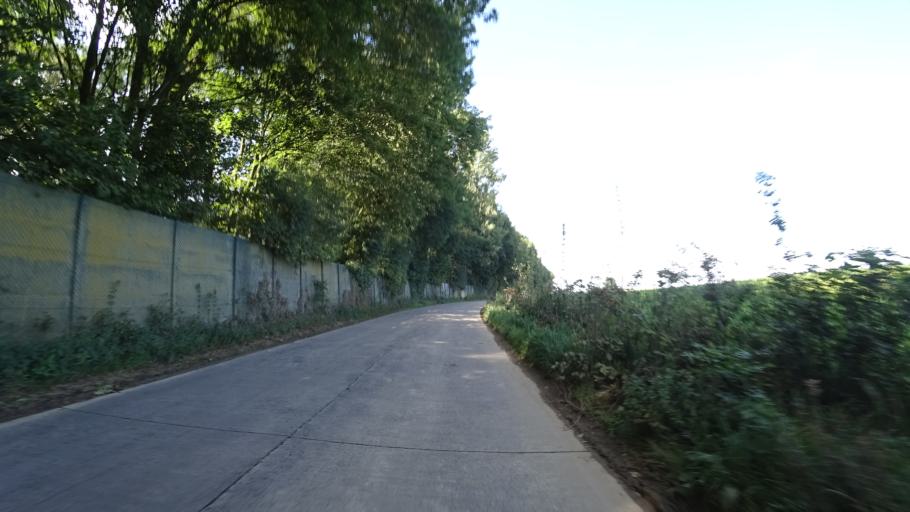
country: BE
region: Wallonia
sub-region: Province du Brabant Wallon
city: Chastre
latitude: 50.5656
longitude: 4.6277
